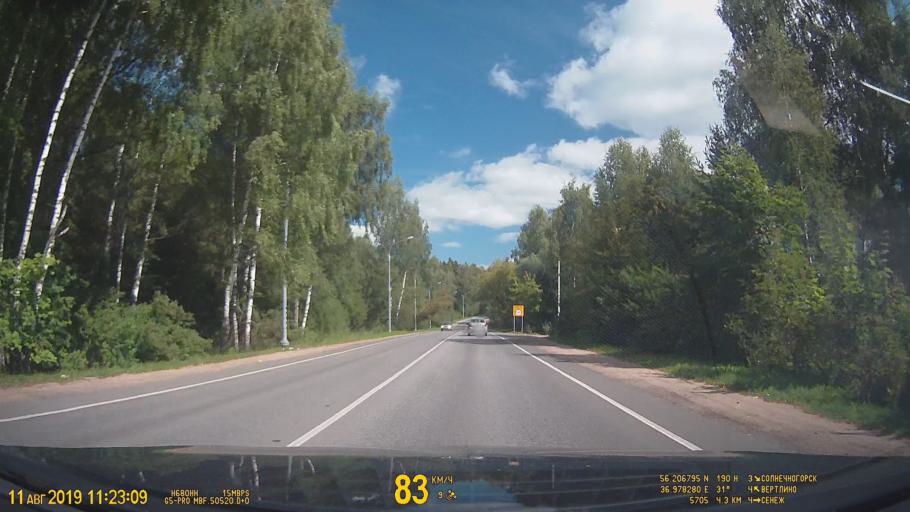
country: RU
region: Moskovskaya
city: Solnechnogorsk
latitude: 56.2070
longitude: 36.9785
